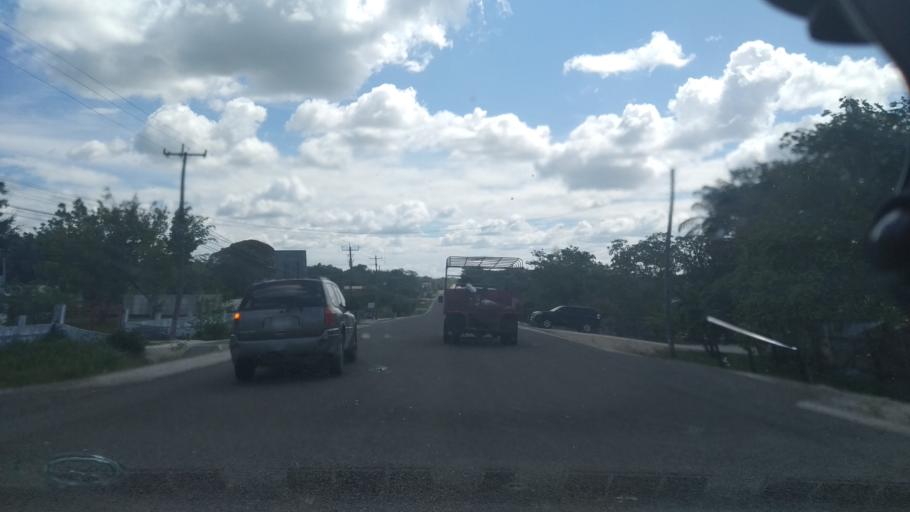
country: BZ
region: Cayo
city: Belmopan
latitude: 17.2540
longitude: -88.8106
